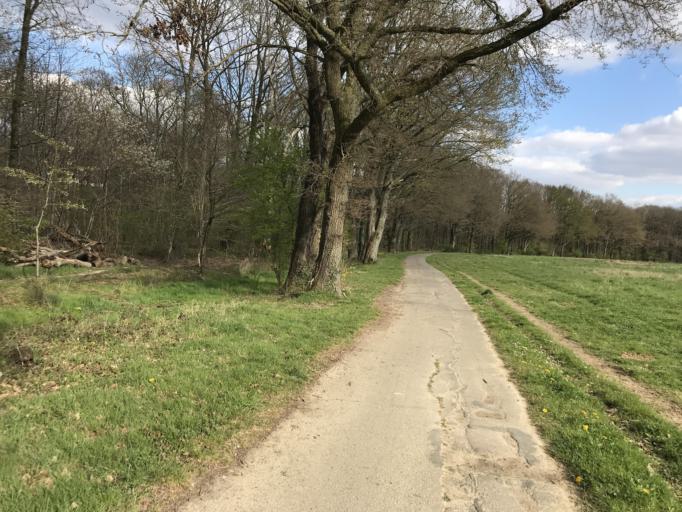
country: FR
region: Ile-de-France
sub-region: Departement de l'Essonne
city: Vauhallan
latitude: 48.7468
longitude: 2.2066
